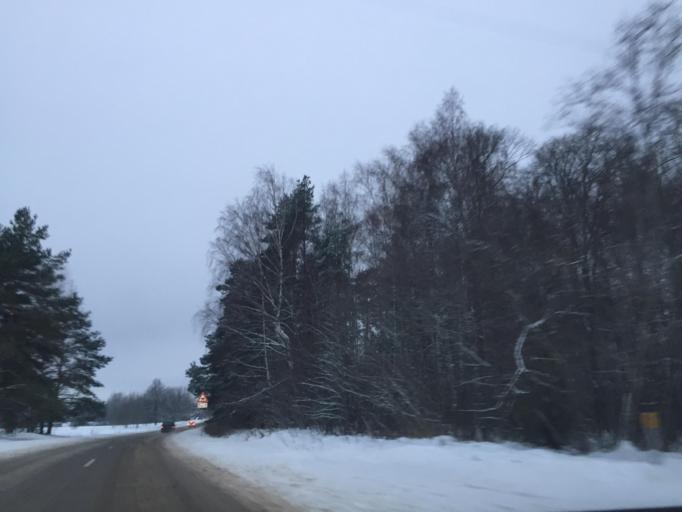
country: LV
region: Smiltene
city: Smiltene
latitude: 57.4358
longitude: 25.7616
